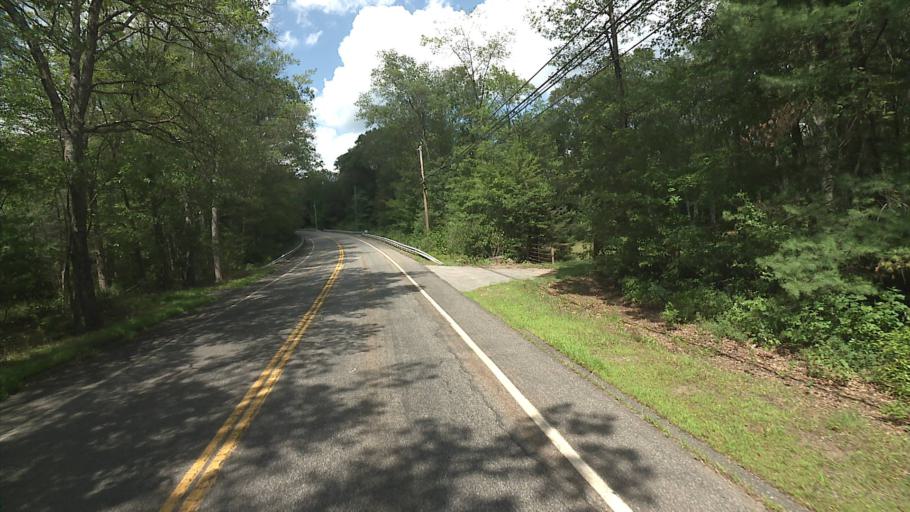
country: US
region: Connecticut
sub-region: Tolland County
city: Storrs
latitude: 41.8823
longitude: -72.1635
